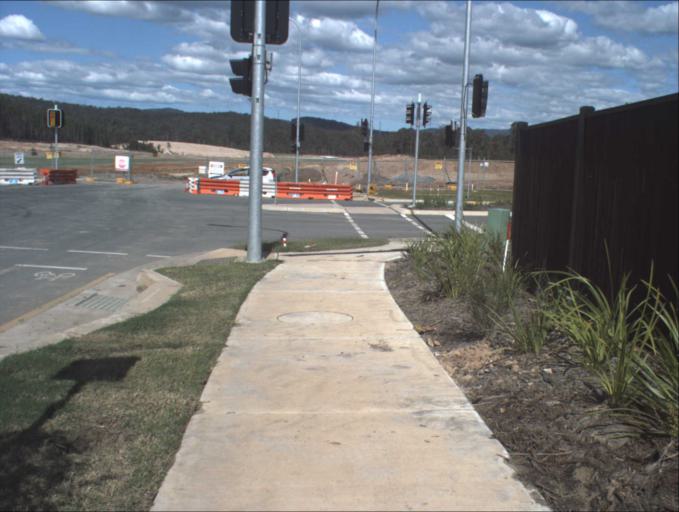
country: AU
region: Queensland
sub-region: Logan
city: Chambers Flat
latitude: -27.8077
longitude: 153.1165
